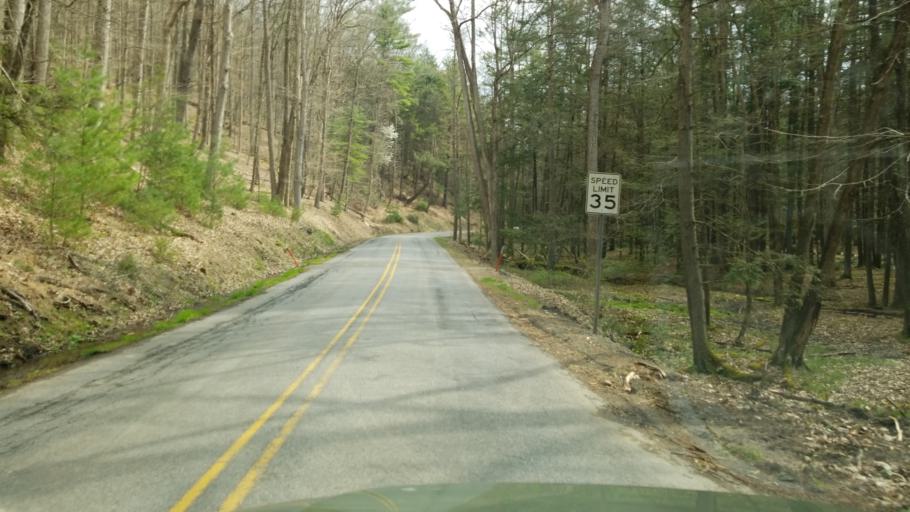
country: US
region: Pennsylvania
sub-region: Cameron County
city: Emporium
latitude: 41.2972
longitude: -78.1090
